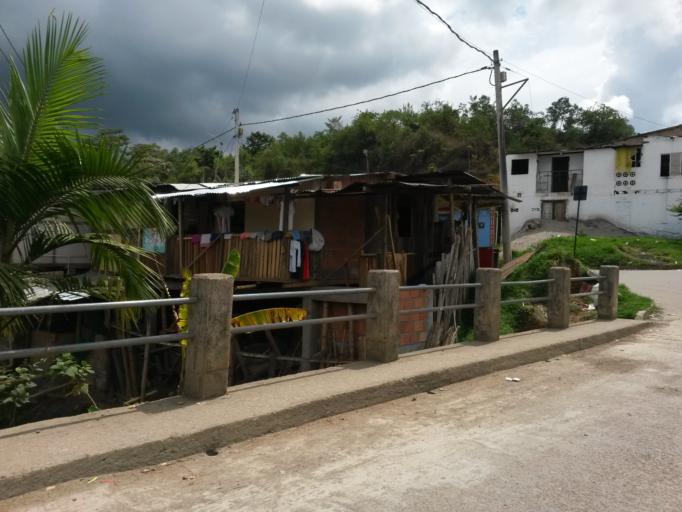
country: CO
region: Huila
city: Isnos
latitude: 1.9339
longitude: -76.2169
